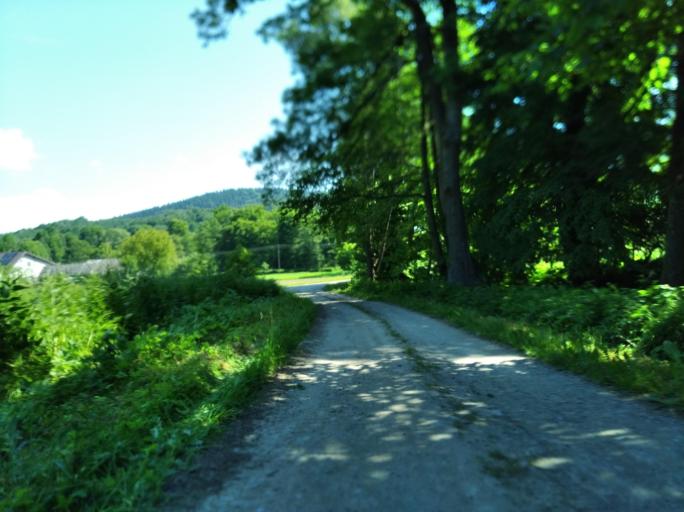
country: PL
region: Subcarpathian Voivodeship
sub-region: Powiat krosnienski
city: Odrzykon
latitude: 49.7796
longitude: 21.7625
